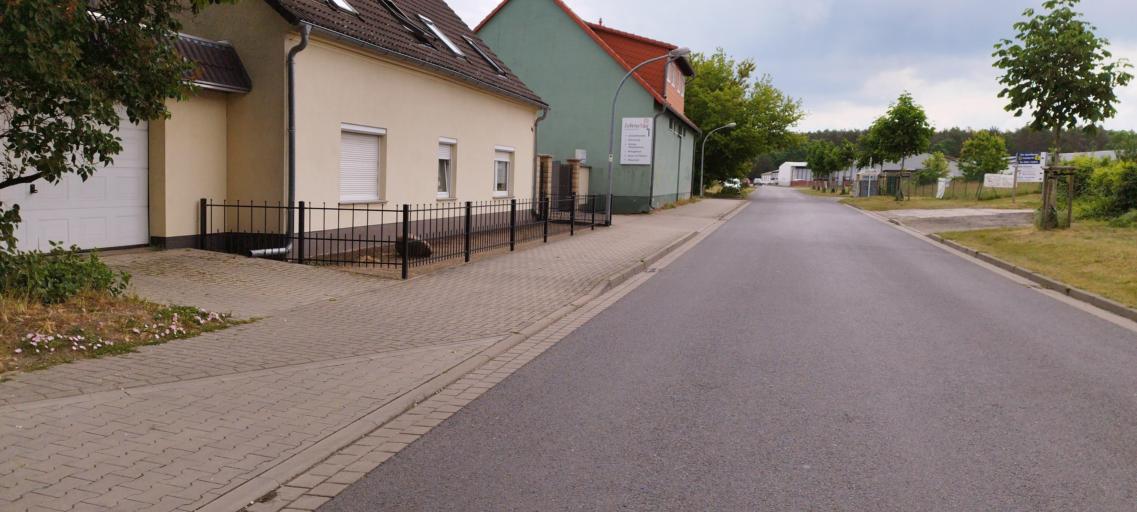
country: DE
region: Brandenburg
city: Furstenwalde
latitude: 52.3658
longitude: 14.0711
